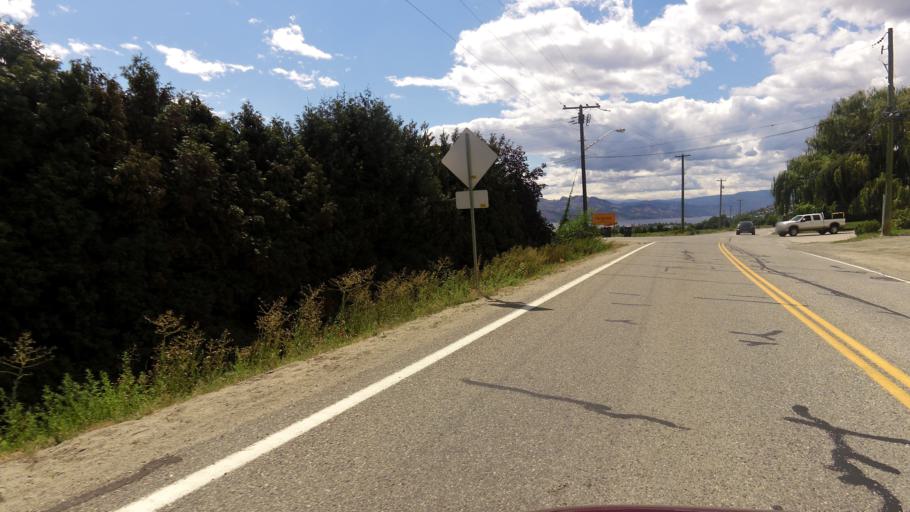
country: CA
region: British Columbia
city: West Kelowna
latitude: 49.8469
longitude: -119.5600
